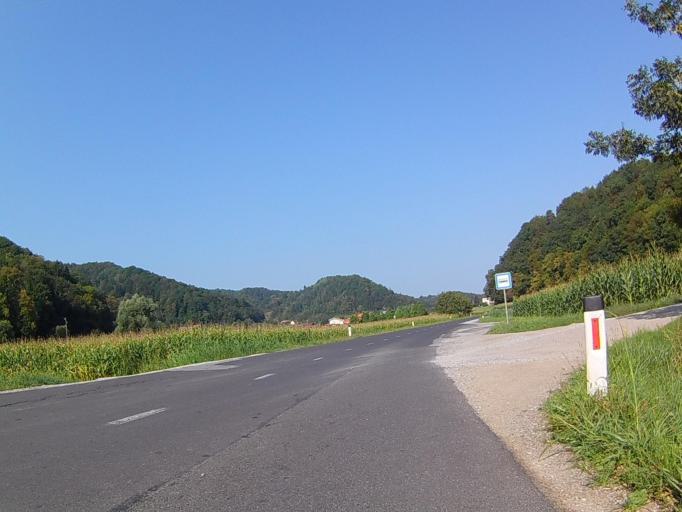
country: SI
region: Kungota
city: Zgornja Kungota
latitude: 46.6389
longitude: 15.6019
